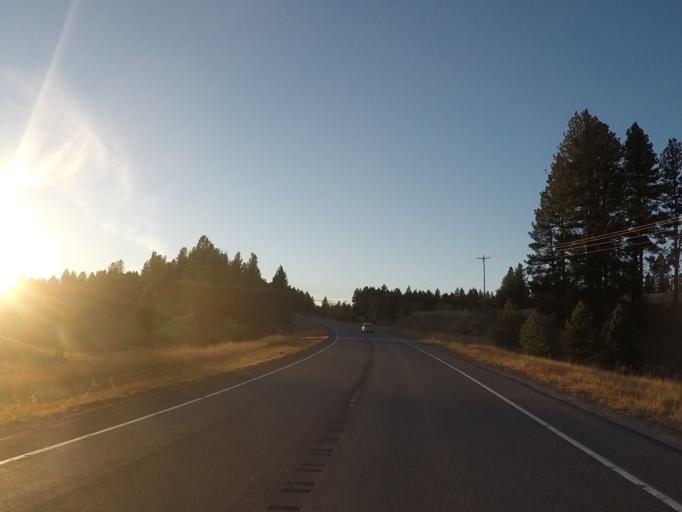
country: US
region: Montana
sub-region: Lewis and Clark County
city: Lincoln
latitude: 47.0074
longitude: -113.0509
